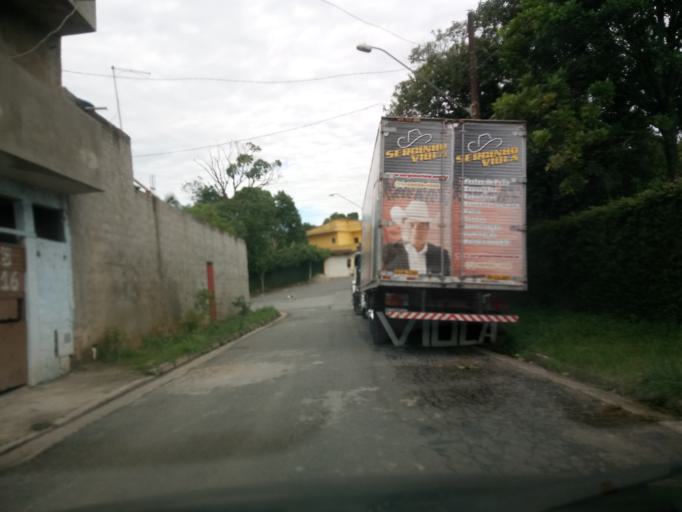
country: BR
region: Sao Paulo
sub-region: Sao Bernardo Do Campo
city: Sao Bernardo do Campo
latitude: -23.8034
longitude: -46.5350
